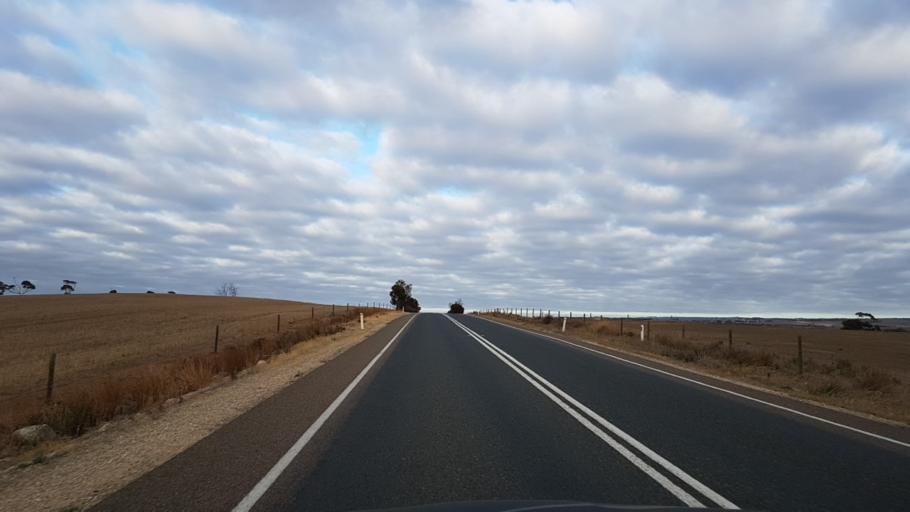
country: AU
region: South Australia
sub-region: Mount Barker
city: Callington
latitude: -35.1968
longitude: 138.9829
